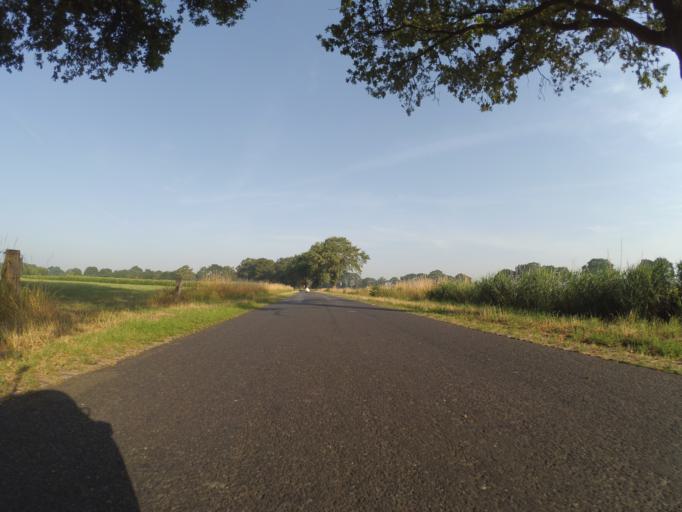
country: NL
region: Overijssel
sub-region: Gemeente Wierden
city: Wierden
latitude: 52.3227
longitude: 6.5988
